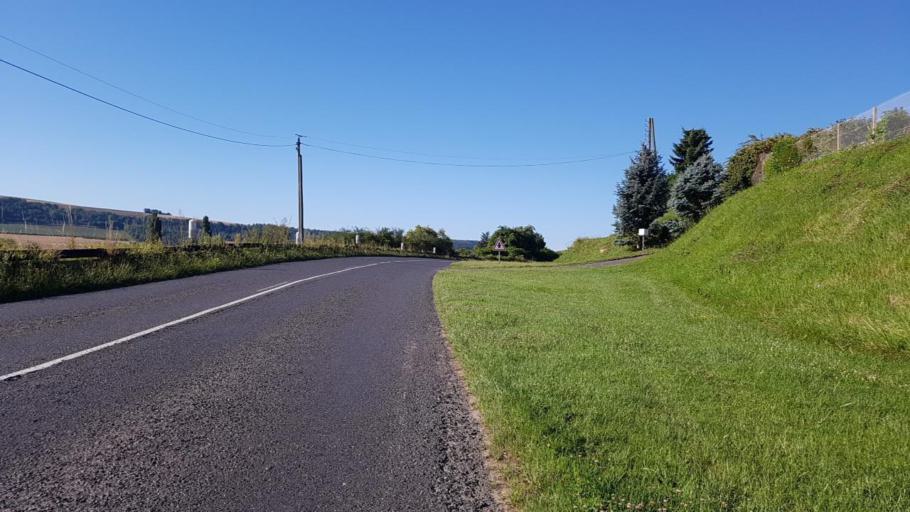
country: FR
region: Picardie
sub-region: Departement de l'Aisne
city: Essomes-sur-Marne
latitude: 49.0111
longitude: 3.3756
